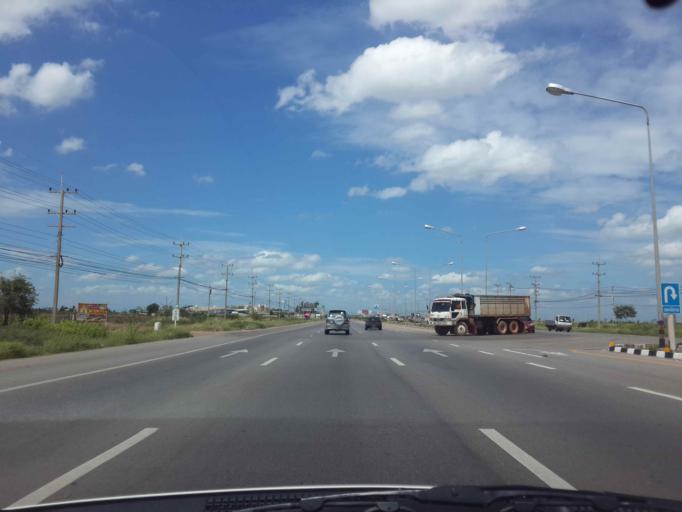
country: TH
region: Samut Songkhram
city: Samut Songkhram
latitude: 13.4615
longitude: 100.0972
